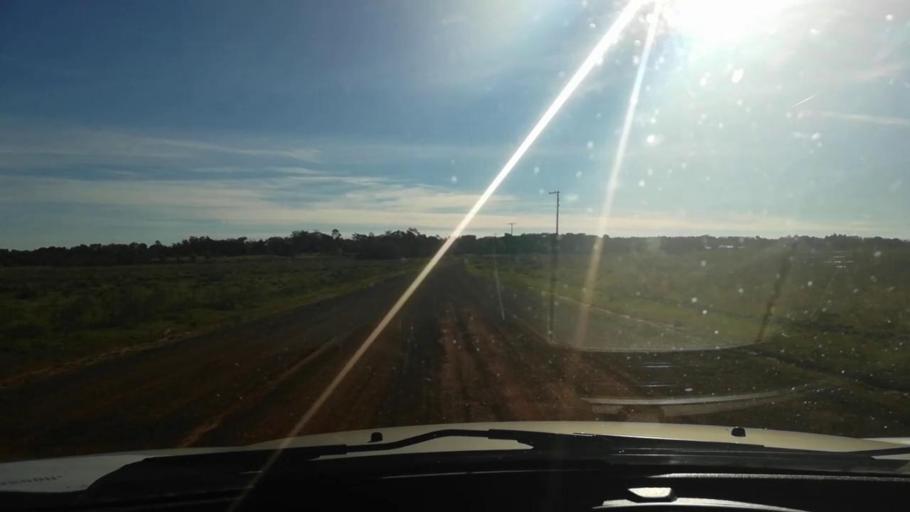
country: PY
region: Caaguazu
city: Coronel Oviedo
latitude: -25.5179
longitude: -56.4121
